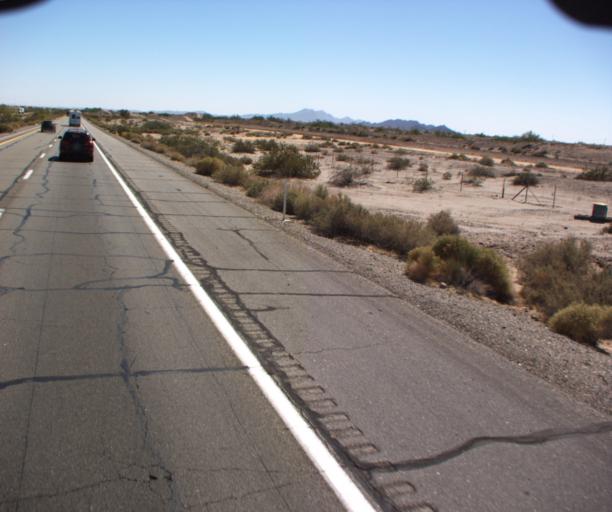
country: US
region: Arizona
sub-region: Yuma County
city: Wellton
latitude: 32.6531
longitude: -114.2277
